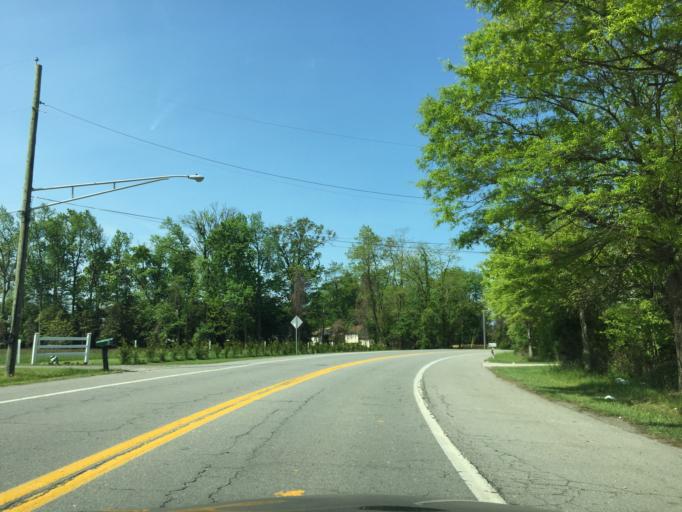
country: US
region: Maryland
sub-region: Baltimore County
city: Bowleys Quarters
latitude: 39.3620
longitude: -76.3643
